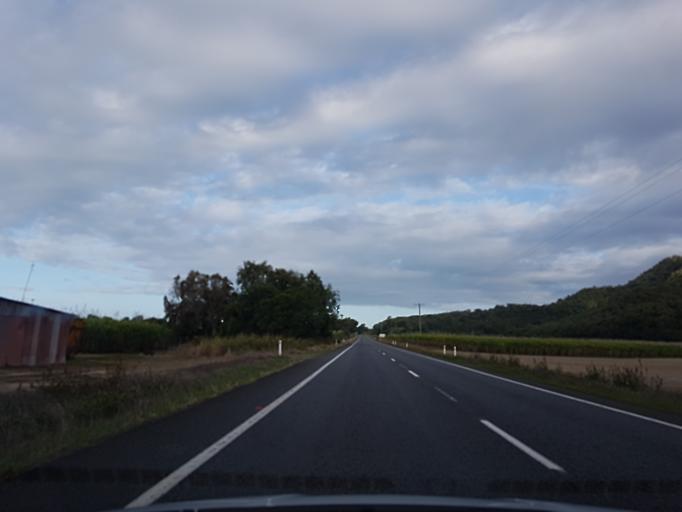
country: AU
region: Queensland
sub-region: Cairns
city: Port Douglas
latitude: -16.5555
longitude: 145.4872
